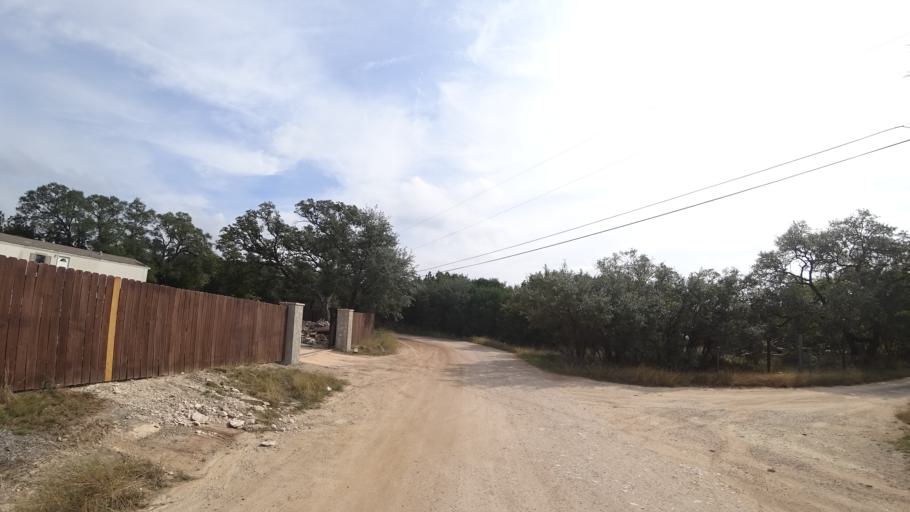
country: US
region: Texas
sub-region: Travis County
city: Hudson Bend
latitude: 30.3849
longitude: -97.9320
